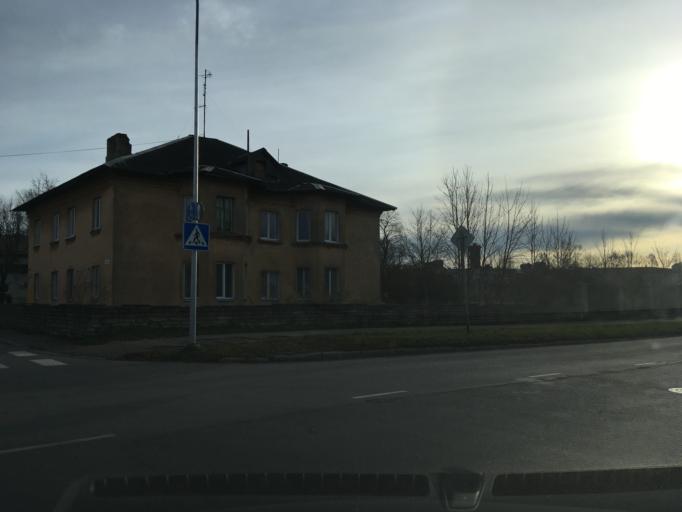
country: EE
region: Ida-Virumaa
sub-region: Narva linn
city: Narva
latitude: 59.3631
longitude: 28.1879
